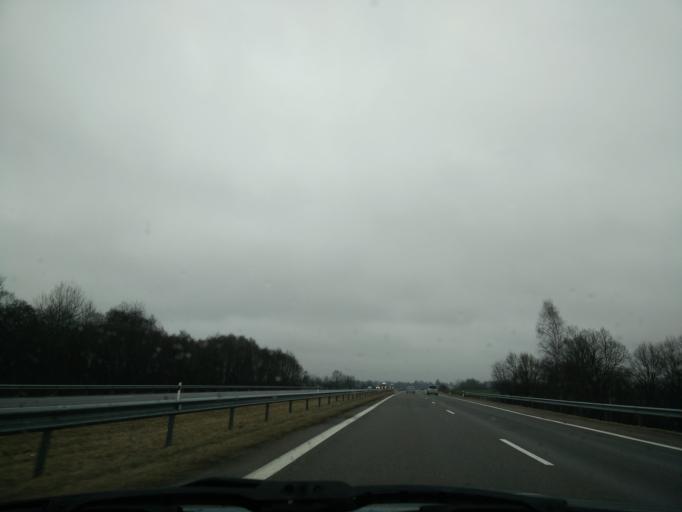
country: LT
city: Skaudvile
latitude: 55.4361
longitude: 22.7386
